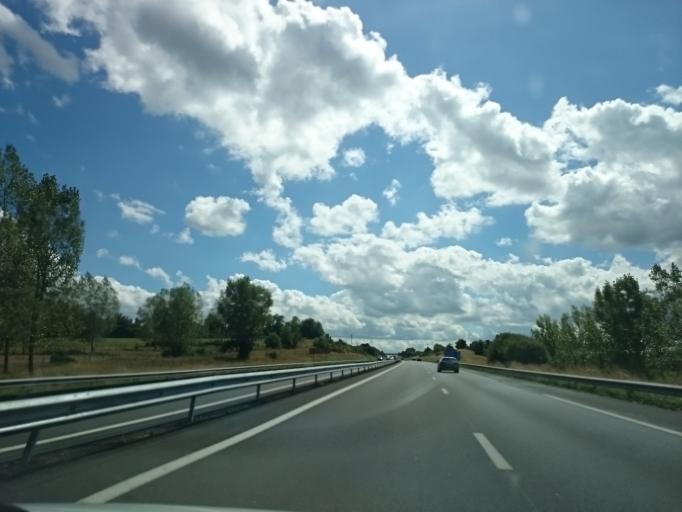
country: FR
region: Pays de la Loire
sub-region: Departement de Maine-et-Loire
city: Durtal
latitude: 47.6513
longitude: -0.2735
